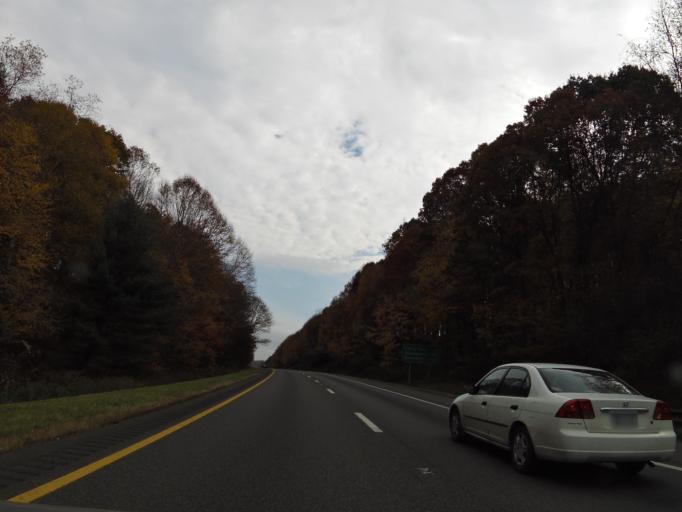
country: US
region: Virginia
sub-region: Carroll County
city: Hillsville
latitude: 36.7327
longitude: -80.7645
